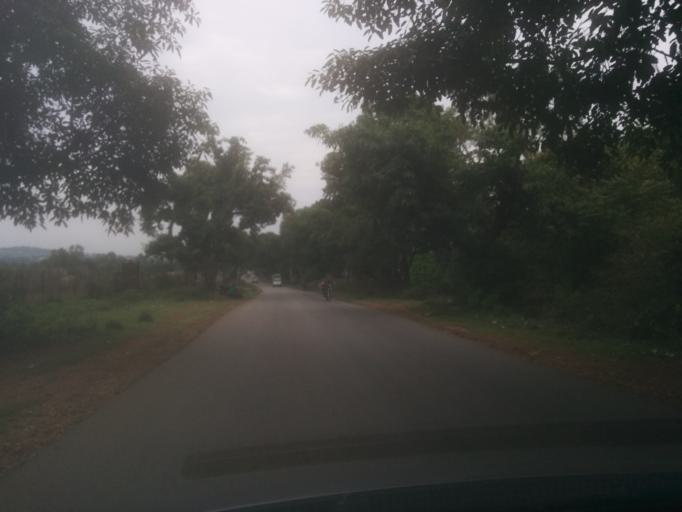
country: IN
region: Karnataka
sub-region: Chikmagalur
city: Chikmagalur
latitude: 13.3613
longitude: 75.7569
